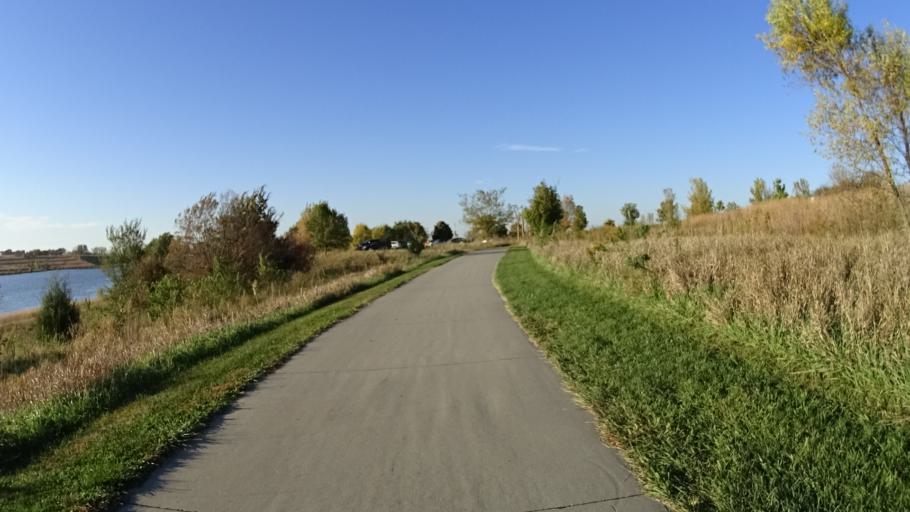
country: US
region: Nebraska
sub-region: Sarpy County
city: Papillion
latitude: 41.1387
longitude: -96.0650
